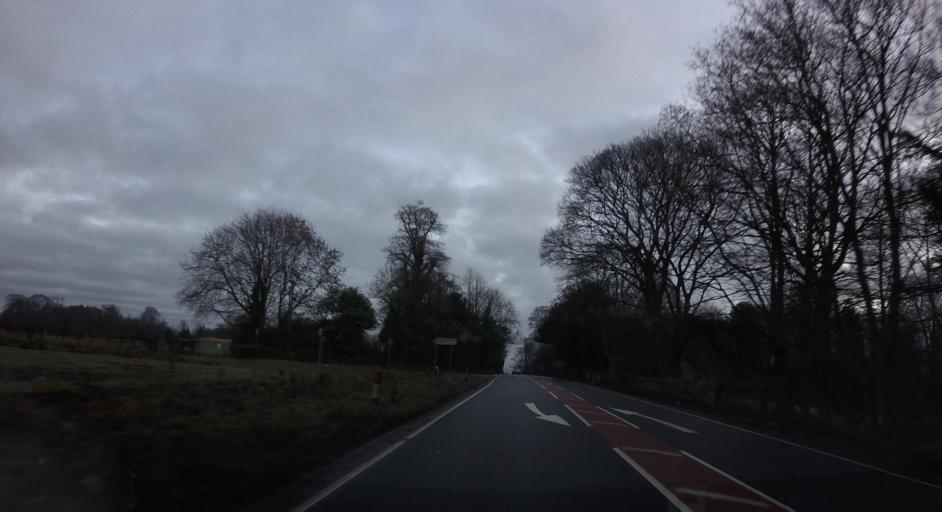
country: GB
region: Scotland
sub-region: Fife
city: Limekilns
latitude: 56.0414
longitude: -3.4716
